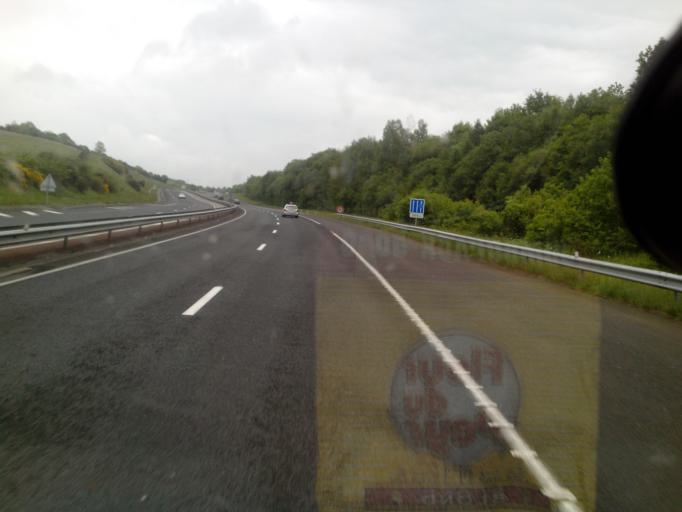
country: FR
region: Lower Normandy
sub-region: Departement de la Manche
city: Tessy-sur-Vire
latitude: 48.9470
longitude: -1.0276
